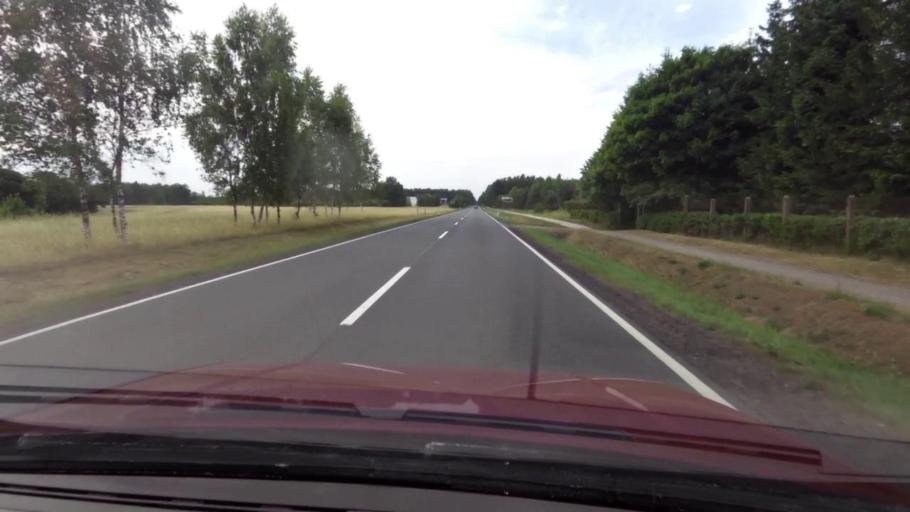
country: PL
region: Pomeranian Voivodeship
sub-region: Powiat bytowski
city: Trzebielino
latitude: 54.2121
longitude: 17.0894
